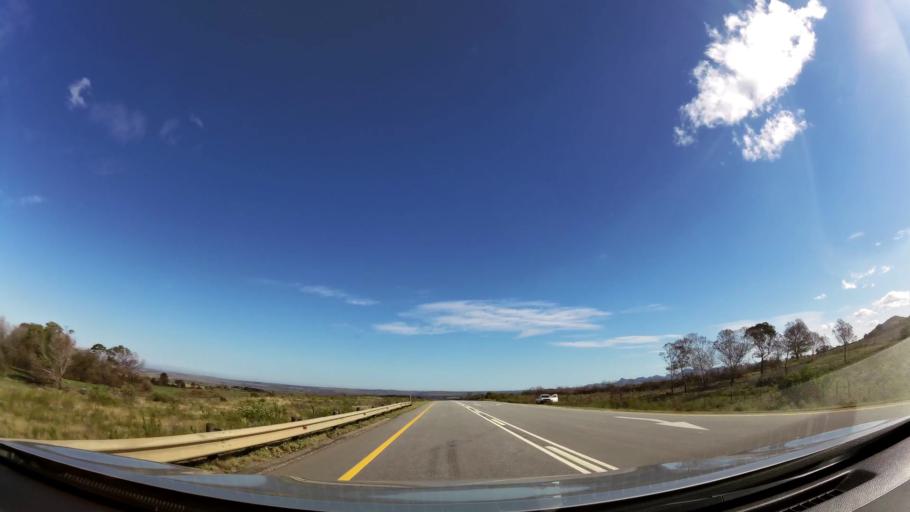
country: ZA
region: Eastern Cape
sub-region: Cacadu District Municipality
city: Kruisfontein
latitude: -33.9986
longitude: 24.6865
